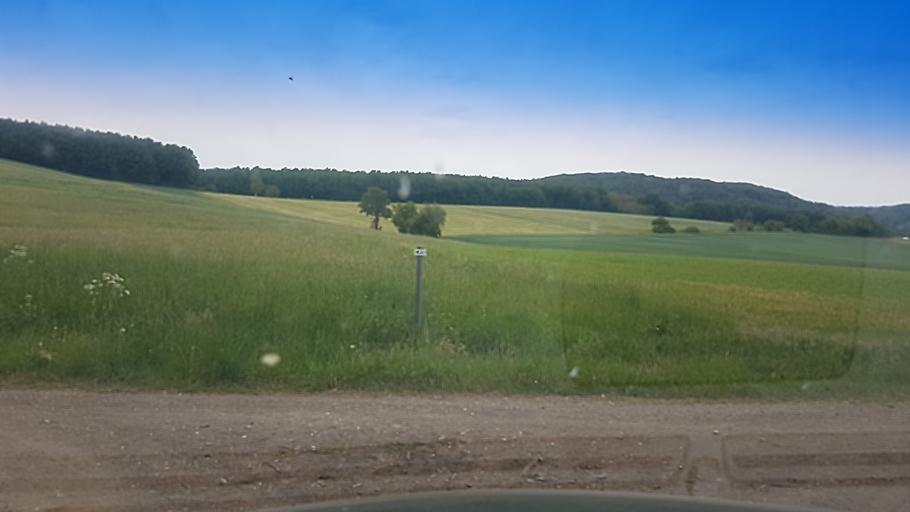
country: DE
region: Bavaria
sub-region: Upper Franconia
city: Buttenheim
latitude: 49.8179
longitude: 11.0474
